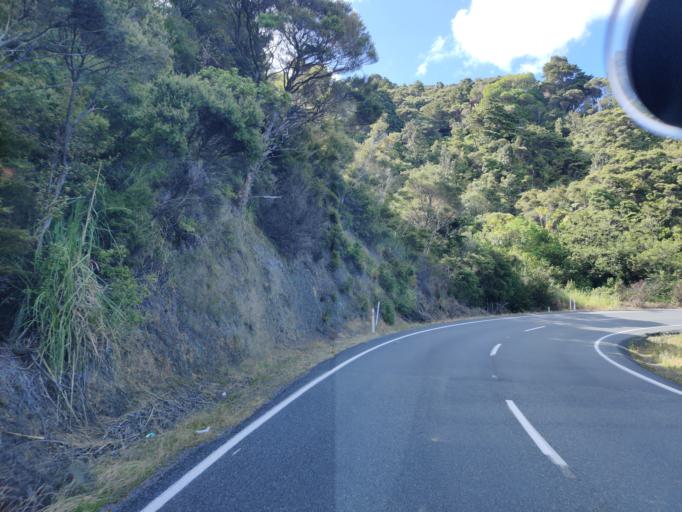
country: NZ
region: Northland
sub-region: Whangarei
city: Ngunguru
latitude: -35.6186
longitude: 174.5155
